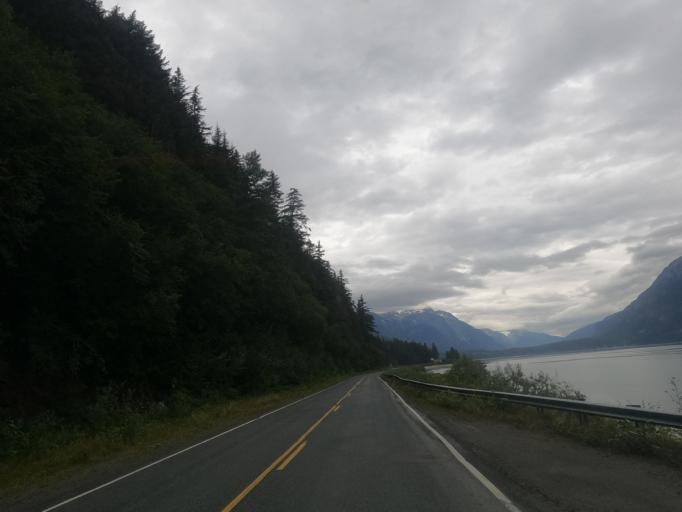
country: US
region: Alaska
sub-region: Haines Borough
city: Haines
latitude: 59.2933
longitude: -135.5023
